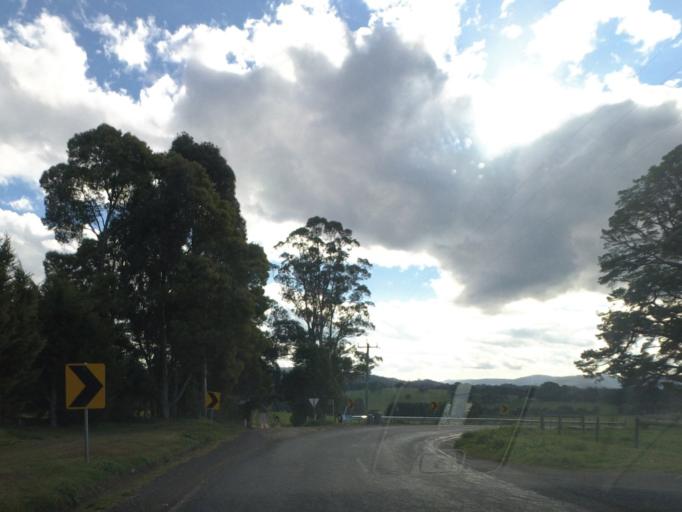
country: AU
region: Victoria
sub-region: Baw Baw
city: Warragul
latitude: -37.9287
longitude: 145.9571
